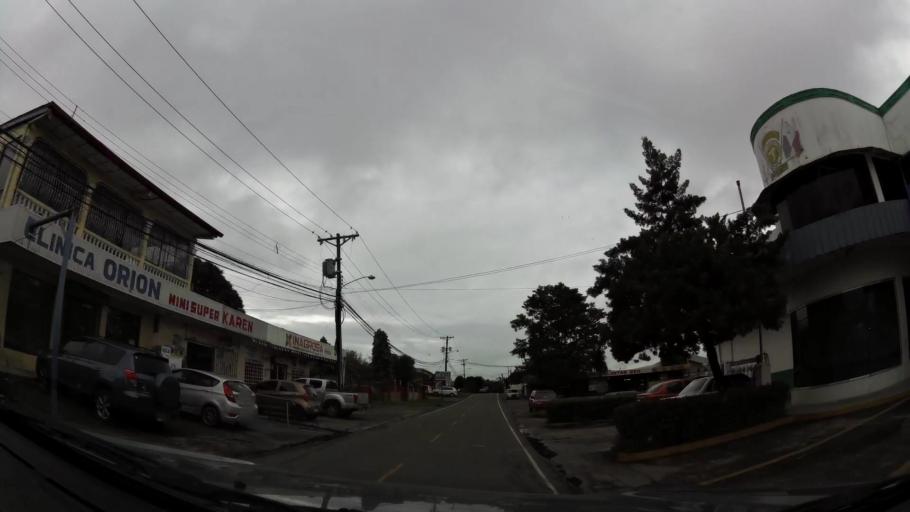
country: PA
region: Chiriqui
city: La Concepcion
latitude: 8.5160
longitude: -82.6188
